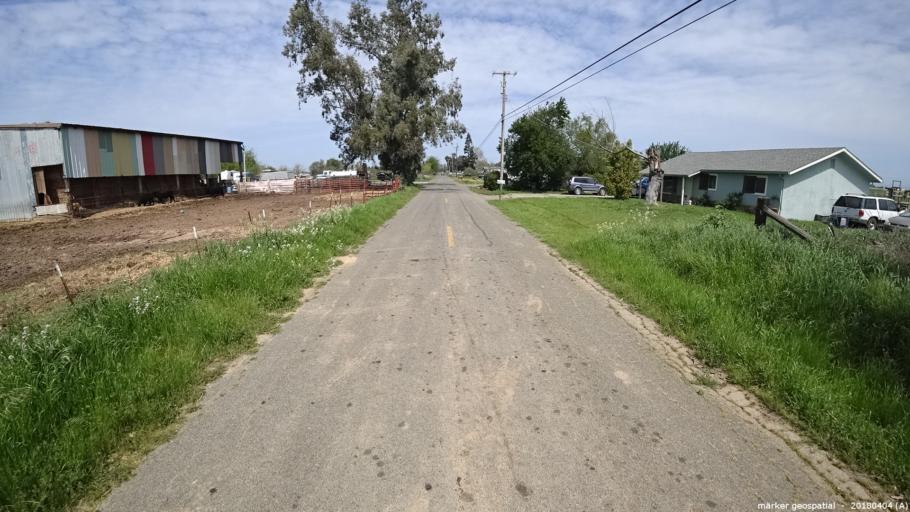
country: US
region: California
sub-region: Sacramento County
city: Herald
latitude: 38.2683
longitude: -121.2542
